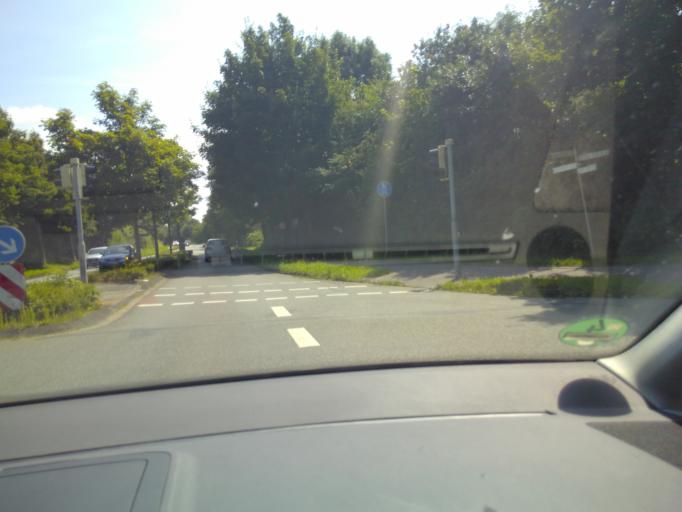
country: DE
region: Lower Saxony
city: Cuxhaven
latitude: 53.8491
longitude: 8.6740
